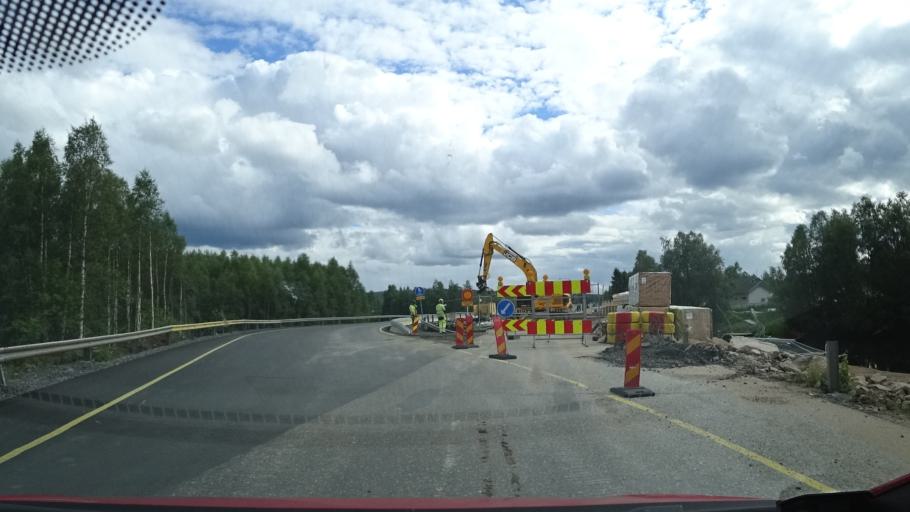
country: FI
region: Lapland
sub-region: Rovaniemi
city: Rovaniemi
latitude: 66.5244
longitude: 25.7445
